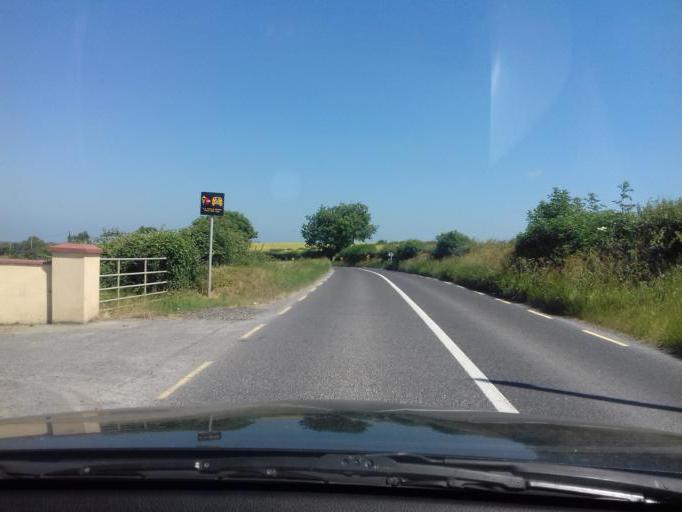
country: IE
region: Leinster
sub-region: An Mhi
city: Stamullin
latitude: 53.5880
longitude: -6.2848
